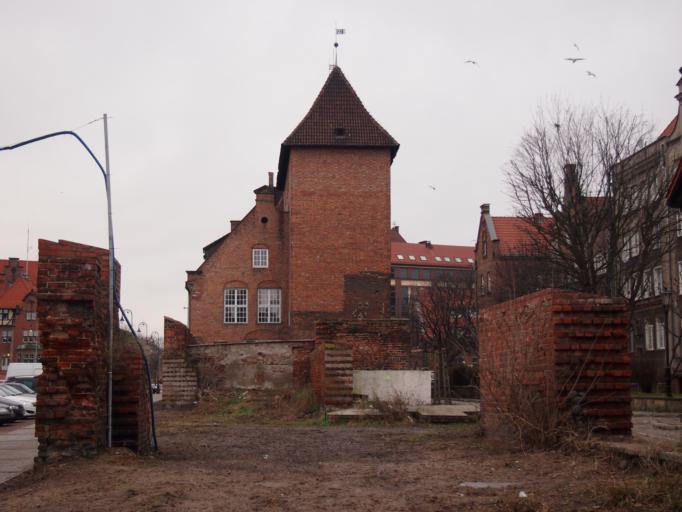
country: PL
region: Pomeranian Voivodeship
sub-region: Gdansk
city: Gdansk
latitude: 54.3480
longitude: 18.6494
